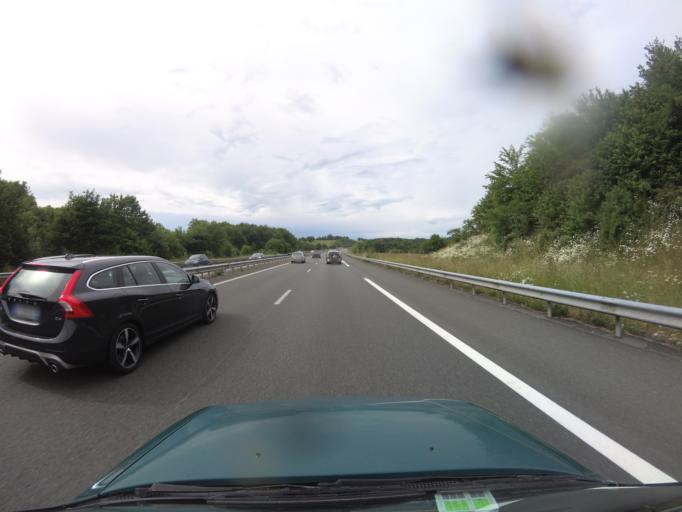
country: FR
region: Pays de la Loire
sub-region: Departement de la Vendee
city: Bournezeau
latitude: 46.6598
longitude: -1.1560
